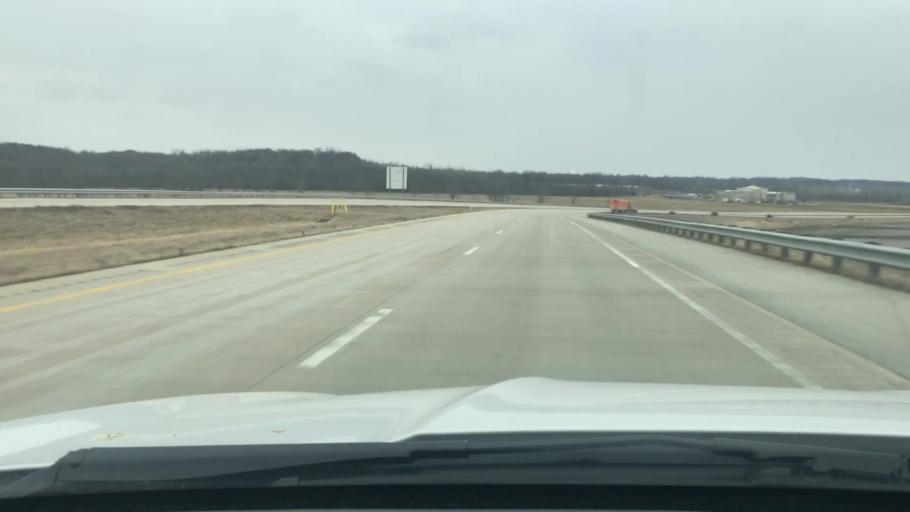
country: US
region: Indiana
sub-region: Cass County
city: Logansport
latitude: 40.7318
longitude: -86.3637
